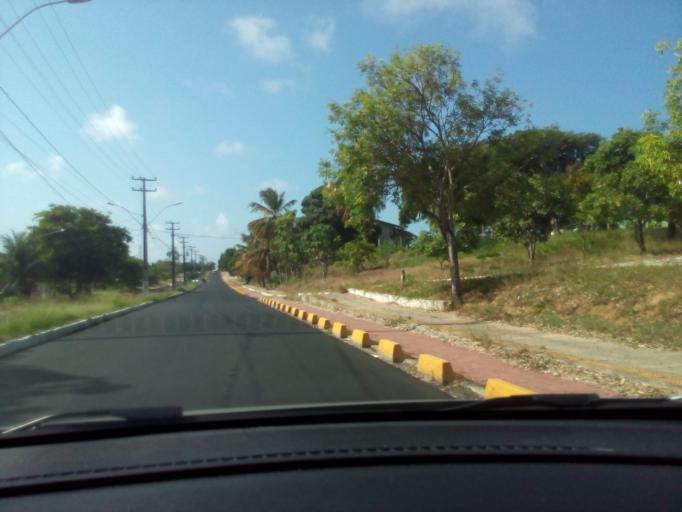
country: BR
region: Rio Grande do Norte
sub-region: Natal
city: Natal
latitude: -5.8415
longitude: -35.2036
